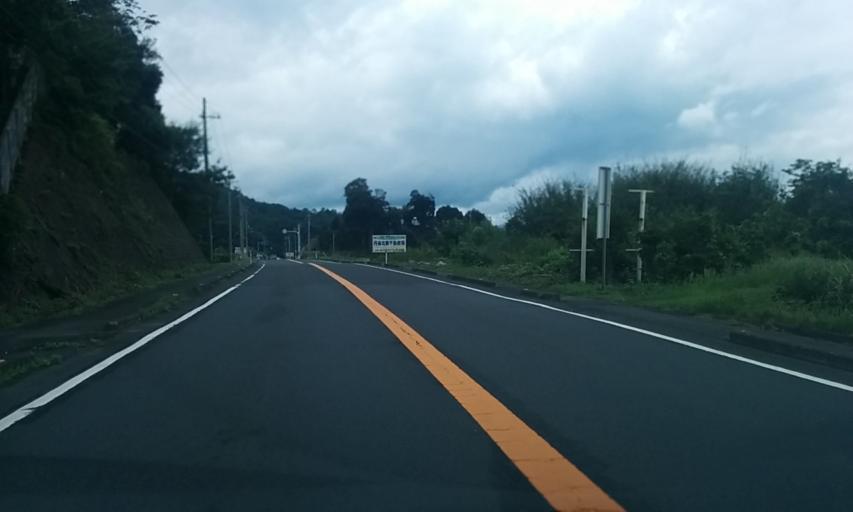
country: JP
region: Kyoto
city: Miyazu
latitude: 35.5379
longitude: 135.2382
